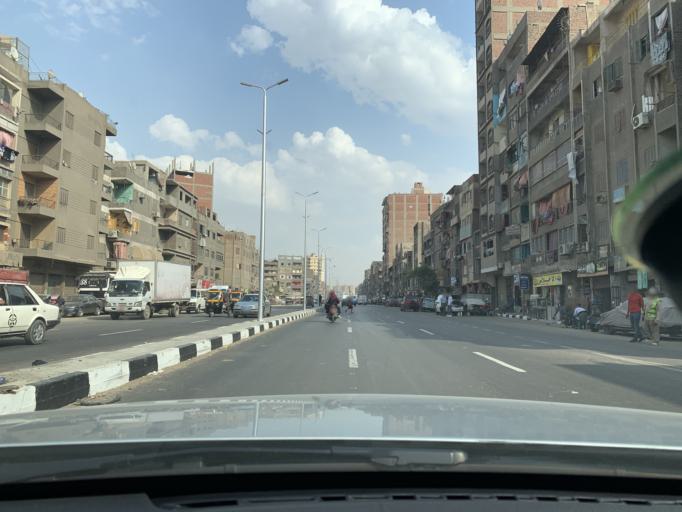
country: EG
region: Muhafazat al Qahirah
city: Cairo
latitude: 30.1244
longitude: 31.2993
